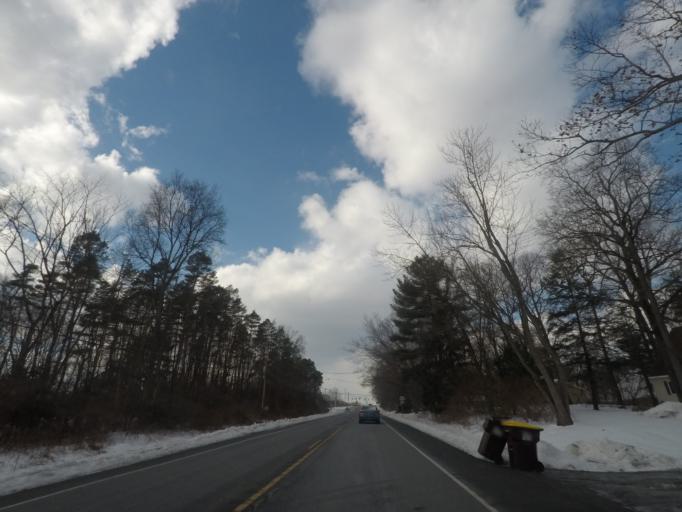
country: US
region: New York
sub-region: Schenectady County
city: East Glenville
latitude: 42.8660
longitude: -73.8844
